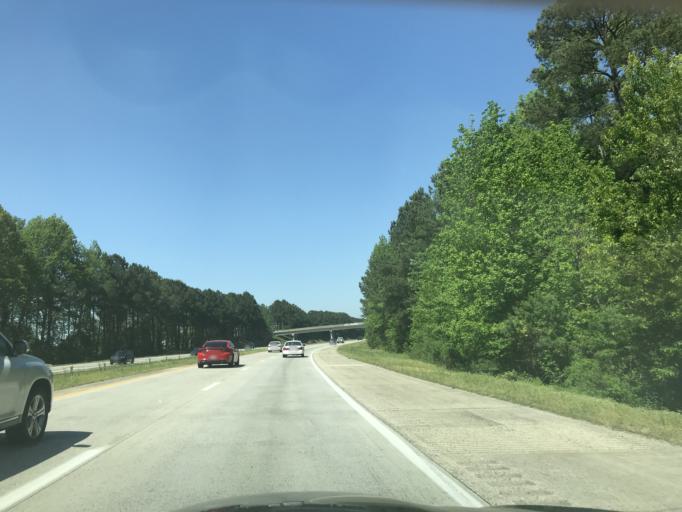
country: US
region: North Carolina
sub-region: Johnston County
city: Clayton
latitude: 35.5502
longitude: -78.5800
